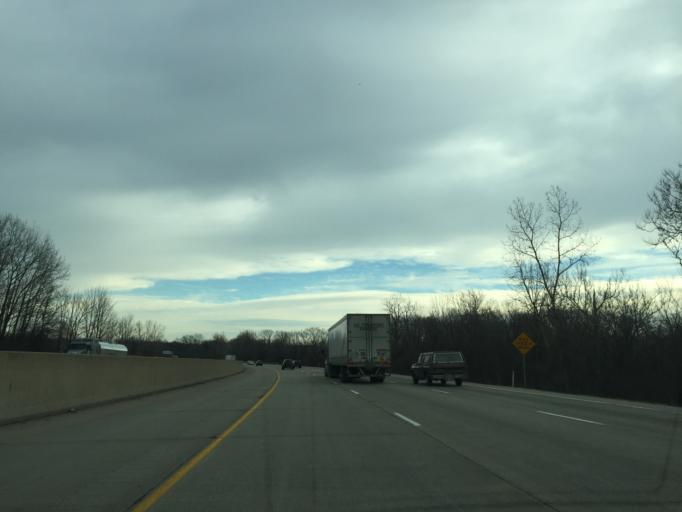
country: US
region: Indiana
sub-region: LaPorte County
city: Trail Creek
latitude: 41.6583
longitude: -86.8758
